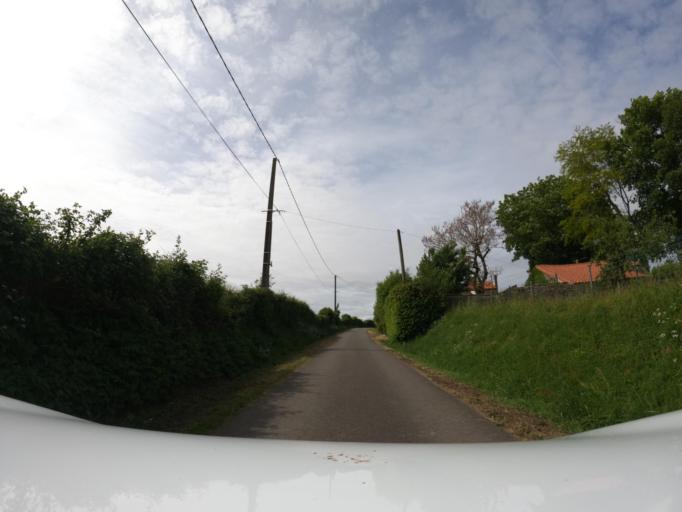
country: FR
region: Pays de la Loire
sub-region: Departement de la Vendee
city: Saint-Hilaire-des-Loges
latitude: 46.4916
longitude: -0.6615
